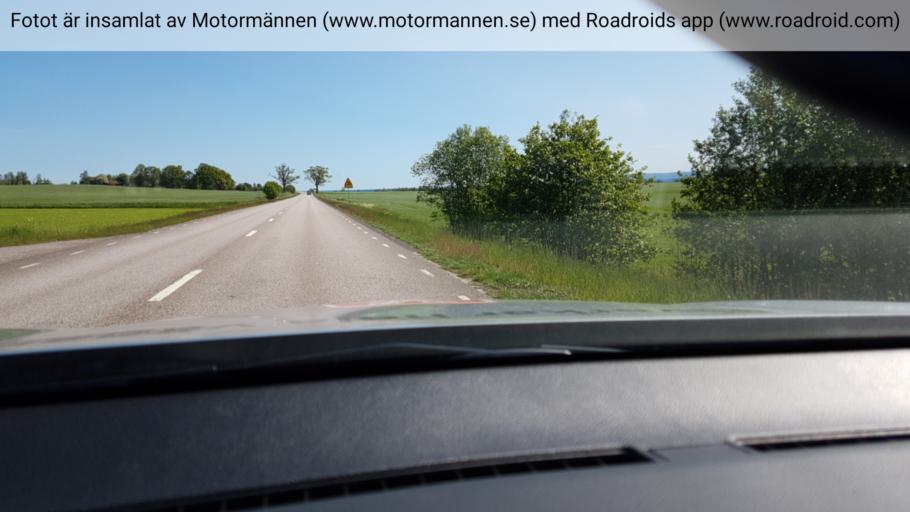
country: SE
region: Vaestra Goetaland
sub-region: Hjo Kommun
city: Hjo
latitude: 58.3252
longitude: 14.3191
